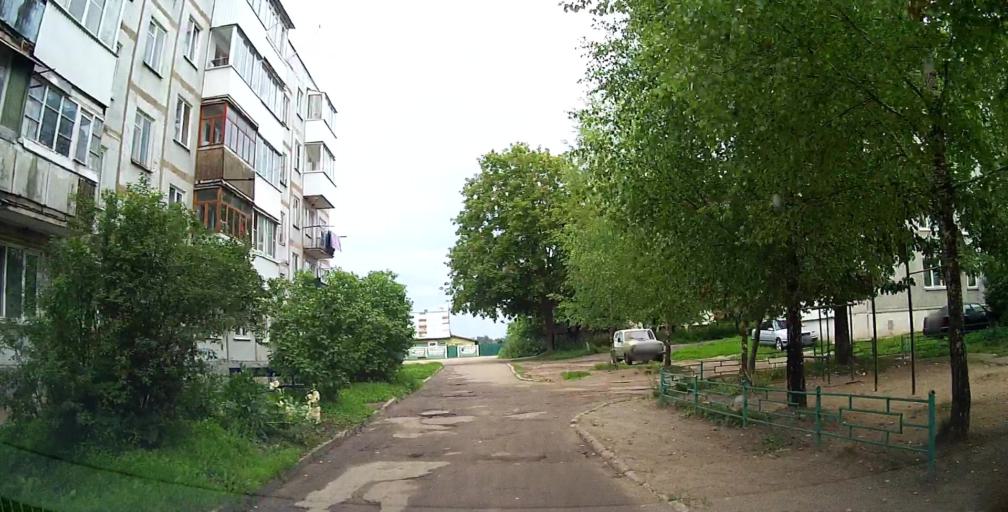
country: RU
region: Smolensk
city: Katyn'
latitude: 54.7716
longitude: 31.6835
